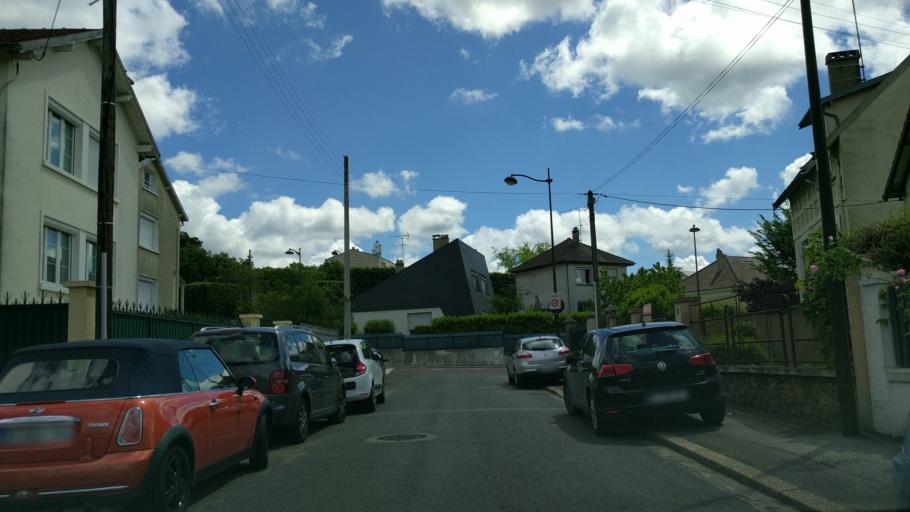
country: FR
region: Ile-de-France
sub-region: Departement des Yvelines
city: Le Chesnay
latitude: 48.8256
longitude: 2.1420
